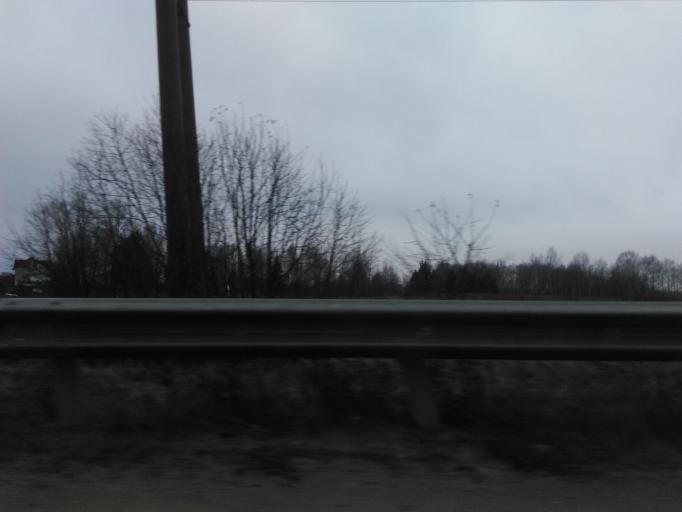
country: RU
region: Moskovskaya
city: Ashukino
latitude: 56.1560
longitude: 37.9625
